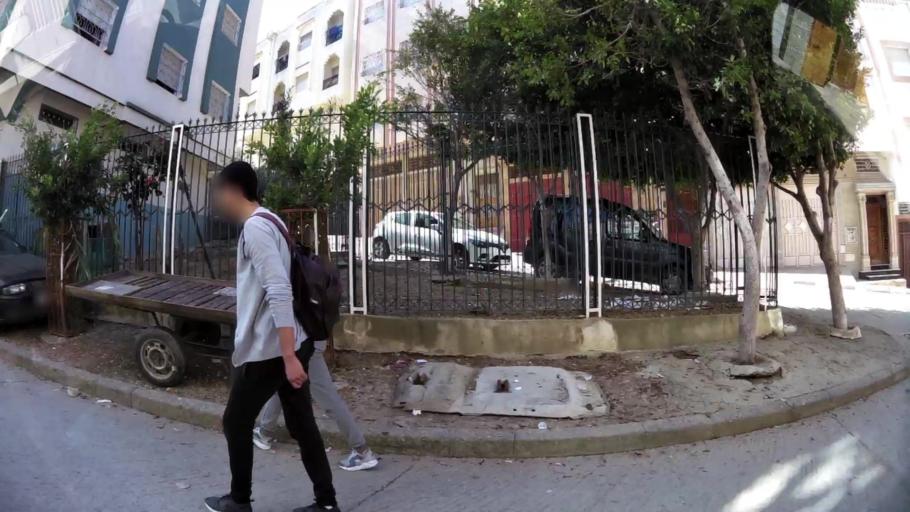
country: MA
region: Tanger-Tetouan
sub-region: Tanger-Assilah
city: Tangier
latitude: 35.7481
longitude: -5.8076
